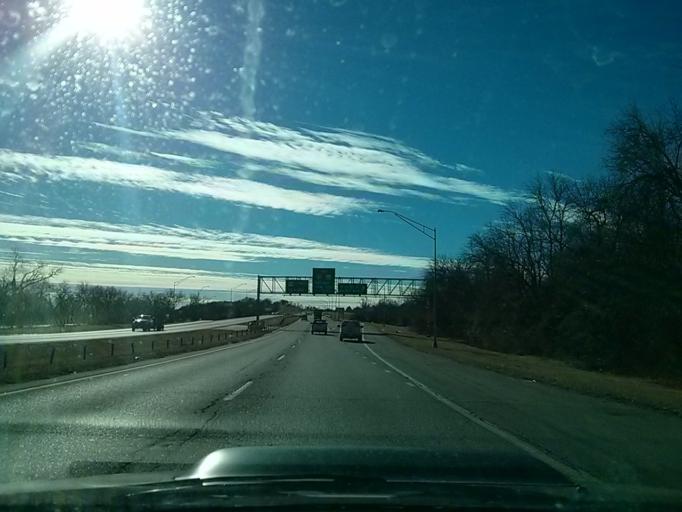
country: US
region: Oklahoma
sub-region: Tulsa County
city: Tulsa
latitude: 36.1080
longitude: -96.0110
